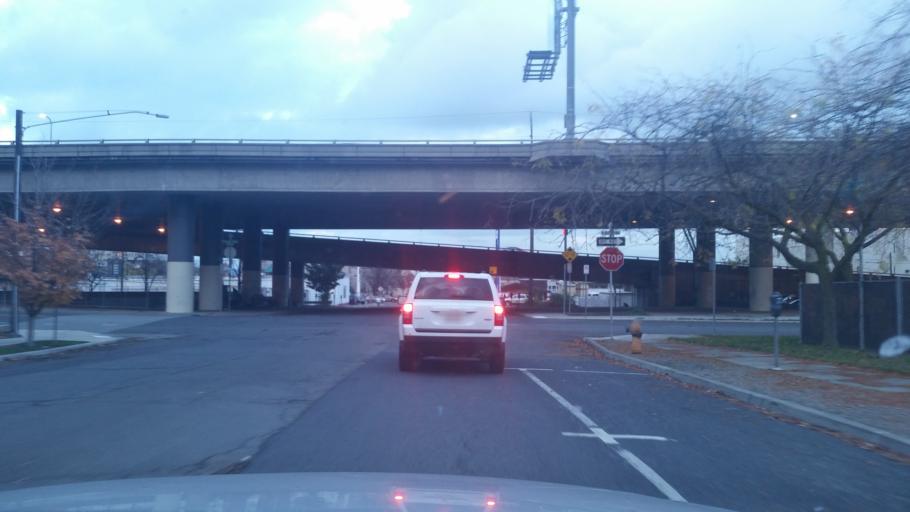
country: US
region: Washington
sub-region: Spokane County
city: Spokane
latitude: 47.6522
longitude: -117.4149
